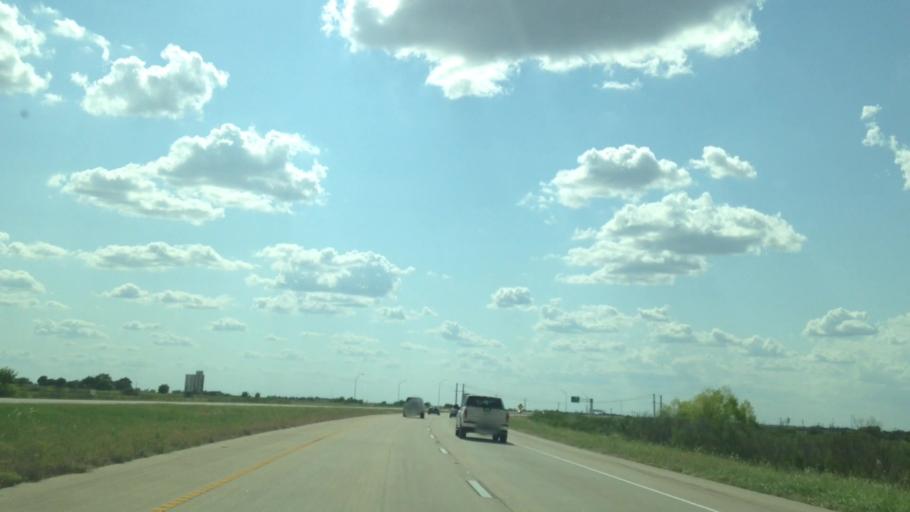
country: US
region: Texas
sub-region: Travis County
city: Onion Creek
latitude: 30.0812
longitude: -97.7241
